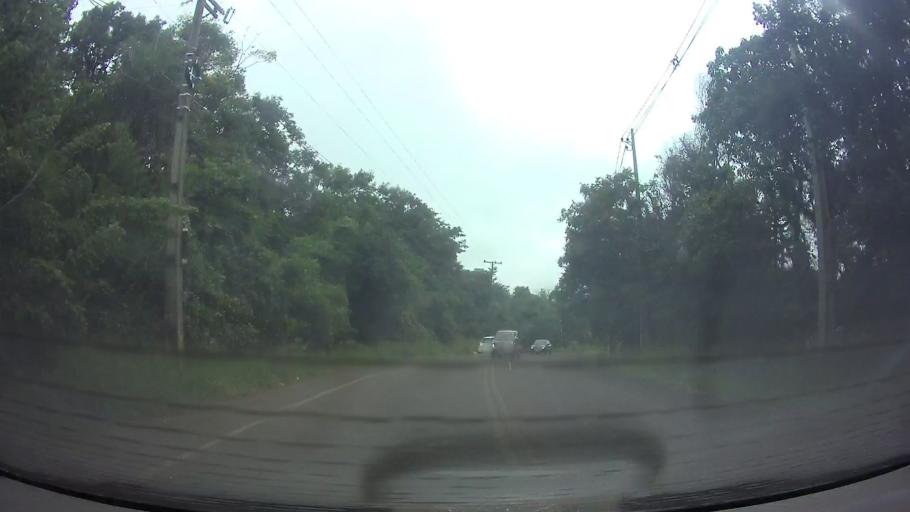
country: PY
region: Cordillera
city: Altos
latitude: -25.2833
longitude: -57.2619
